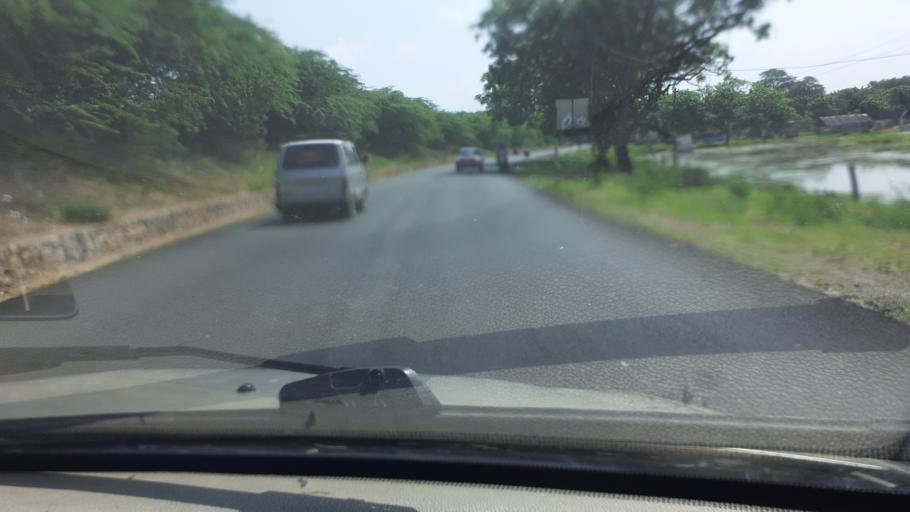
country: IN
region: Tamil Nadu
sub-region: Thoothukkudi
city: Alwar Tirunagari
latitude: 8.6110
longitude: 77.9252
